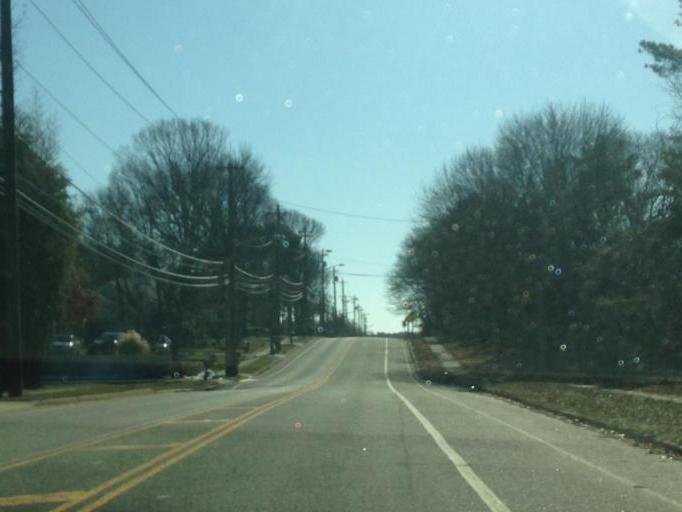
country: US
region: New York
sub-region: Suffolk County
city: Holtsville
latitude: 40.7965
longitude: -73.0432
